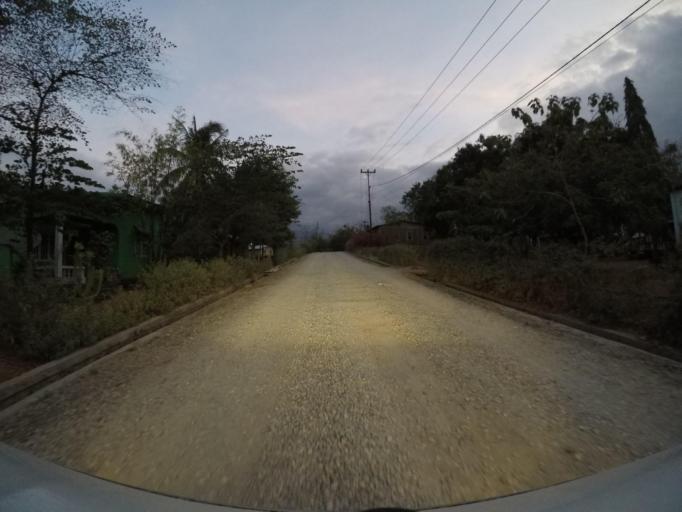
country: TL
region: Bobonaro
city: Maliana
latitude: -8.9791
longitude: 125.2185
